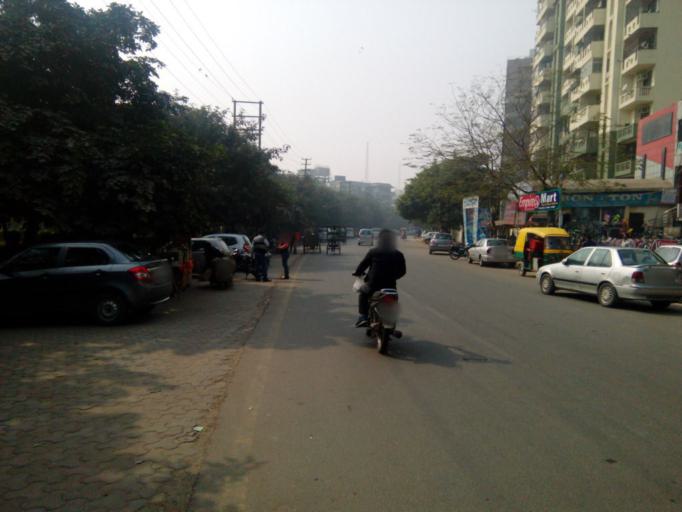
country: IN
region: Uttar Pradesh
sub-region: Gautam Buddha Nagar
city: Noida
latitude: 28.6354
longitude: 77.3657
